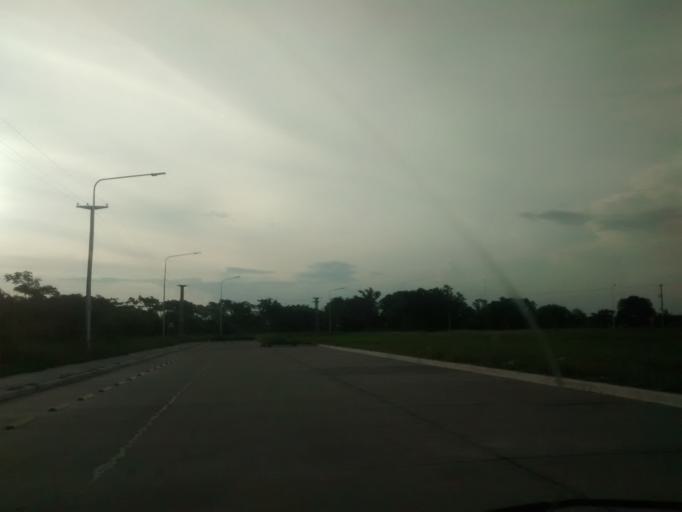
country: AR
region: Chaco
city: Resistencia
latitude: -27.4333
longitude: -58.9719
